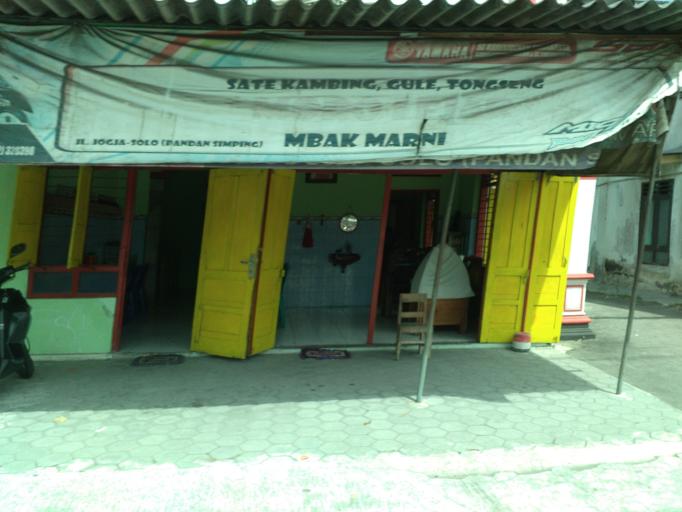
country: ID
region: Central Java
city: Jogonalan
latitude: -7.7409
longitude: 110.5325
